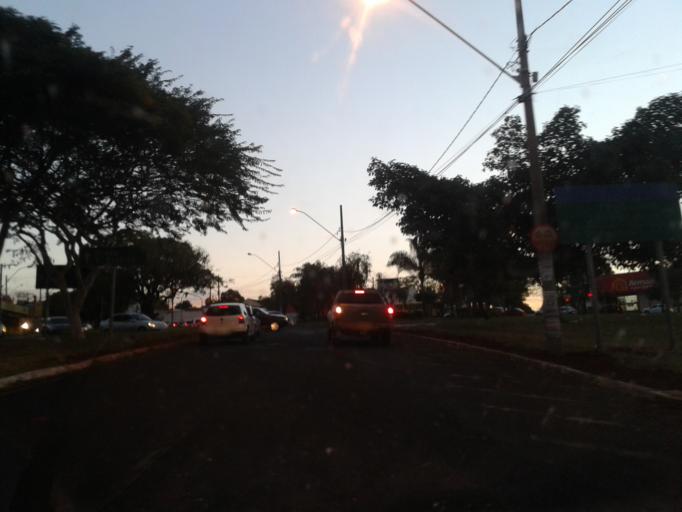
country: BR
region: Minas Gerais
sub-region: Uberlandia
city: Uberlandia
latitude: -18.9293
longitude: -48.3003
